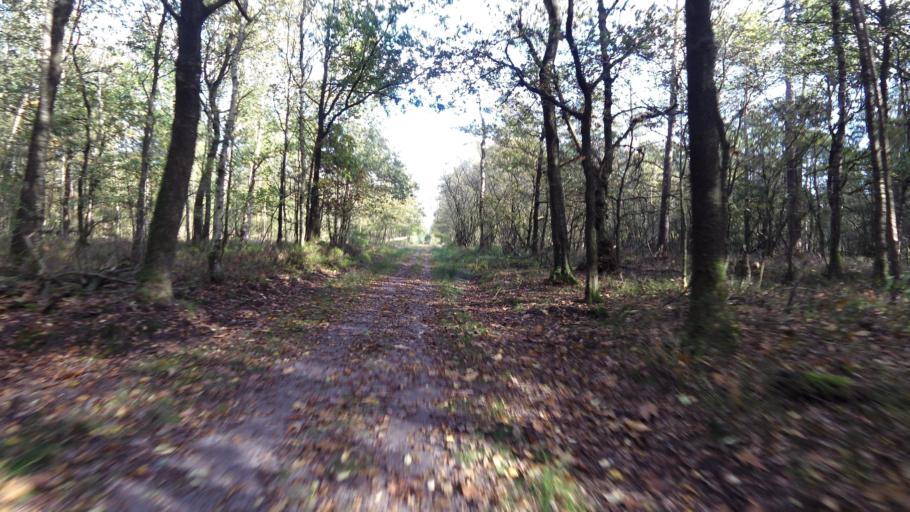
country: NL
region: Gelderland
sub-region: Gemeente Nunspeet
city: Nunspeet
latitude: 52.3370
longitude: 5.8454
